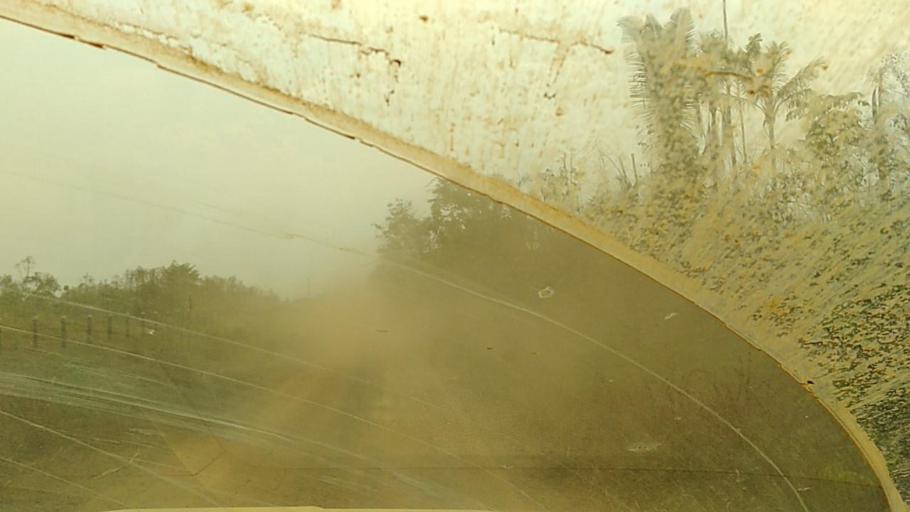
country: BR
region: Rondonia
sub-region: Porto Velho
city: Porto Velho
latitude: -8.7729
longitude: -63.2007
